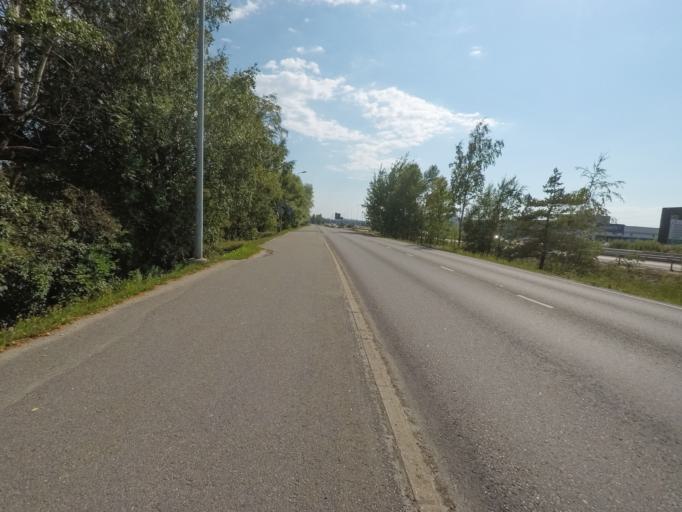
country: FI
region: Uusimaa
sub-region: Helsinki
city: Vantaa
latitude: 60.2775
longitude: 24.9782
